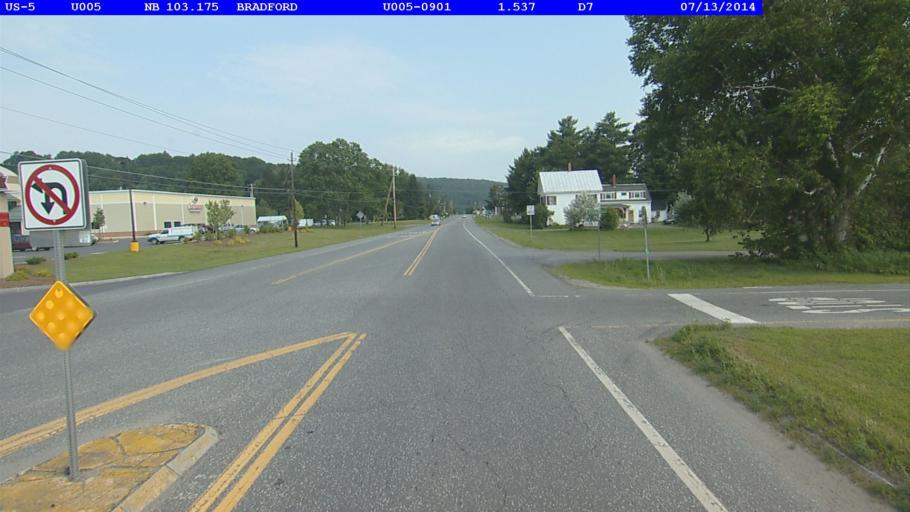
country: US
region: New Hampshire
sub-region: Grafton County
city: Haverhill
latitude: 43.9836
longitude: -72.1215
